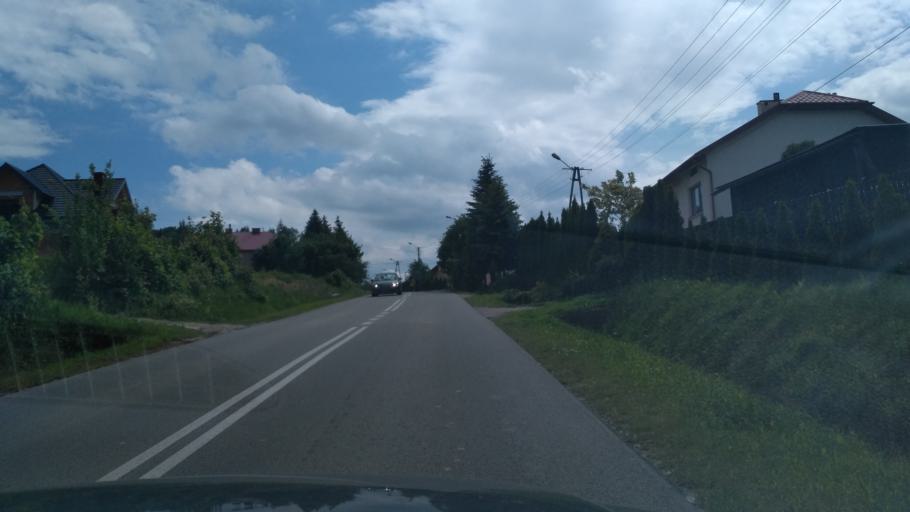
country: PL
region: Subcarpathian Voivodeship
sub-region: Powiat ropczycko-sedziszowski
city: Ropczyce
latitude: 50.0398
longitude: 21.6194
